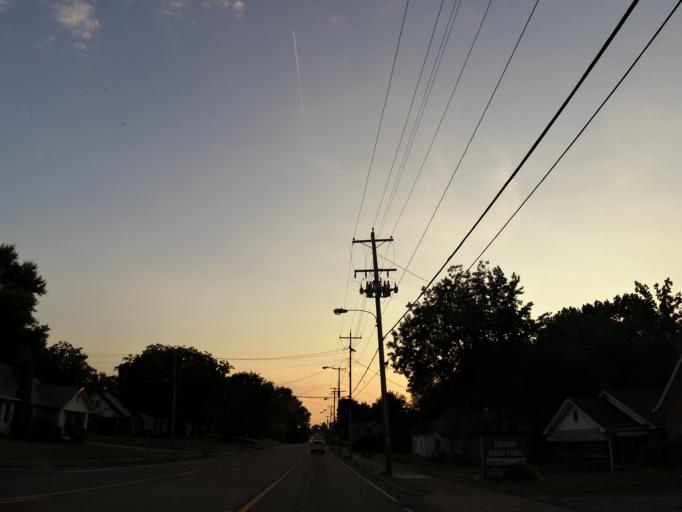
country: US
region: Tennessee
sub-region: Henry County
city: Paris
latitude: 36.3019
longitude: -88.3151
